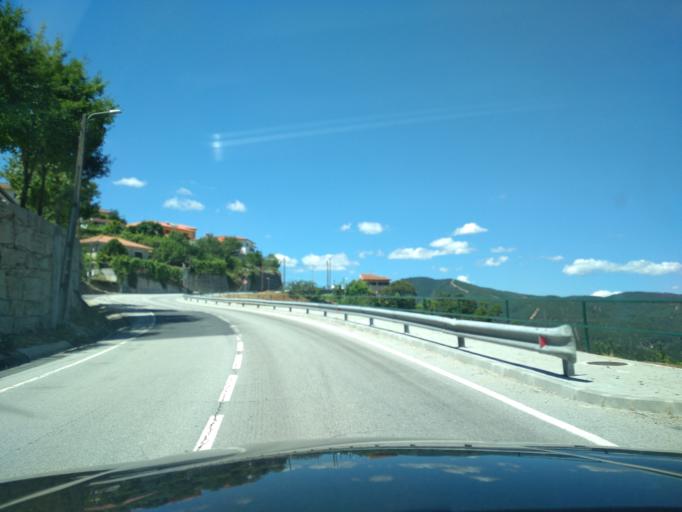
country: PT
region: Vila Real
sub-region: Ribeira de Pena
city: Sobreira
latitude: 41.5252
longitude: -7.7886
